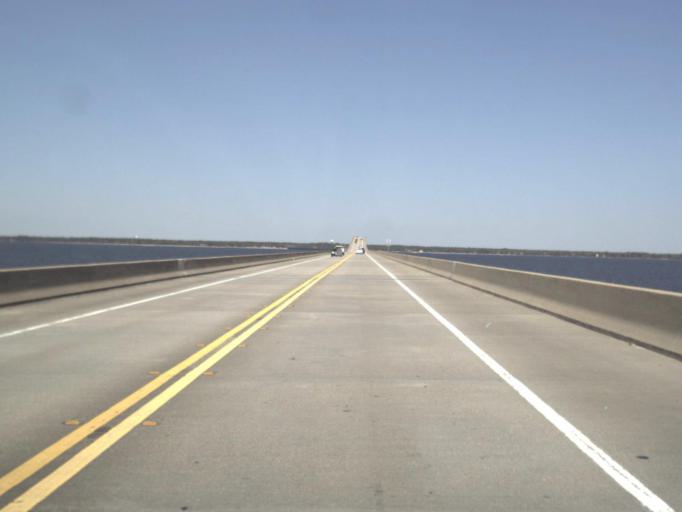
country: US
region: Florida
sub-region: Walton County
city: Miramar Beach
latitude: 30.4210
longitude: -86.4208
